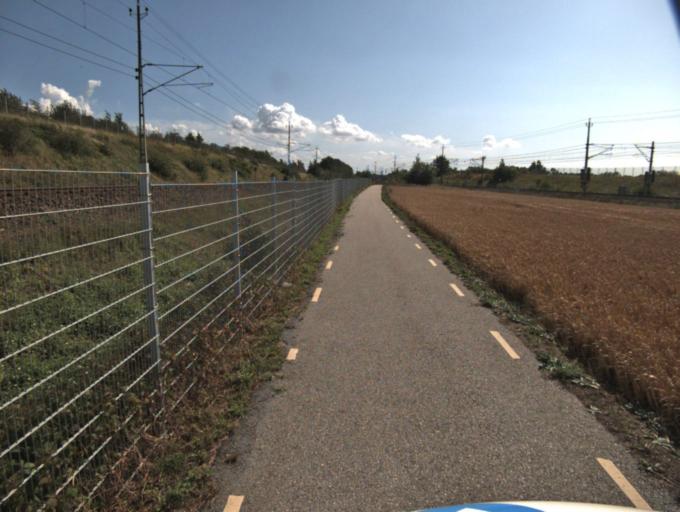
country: SE
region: Skane
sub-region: Kavlinge Kommun
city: Kaevlinge
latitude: 55.8085
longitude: 13.1097
